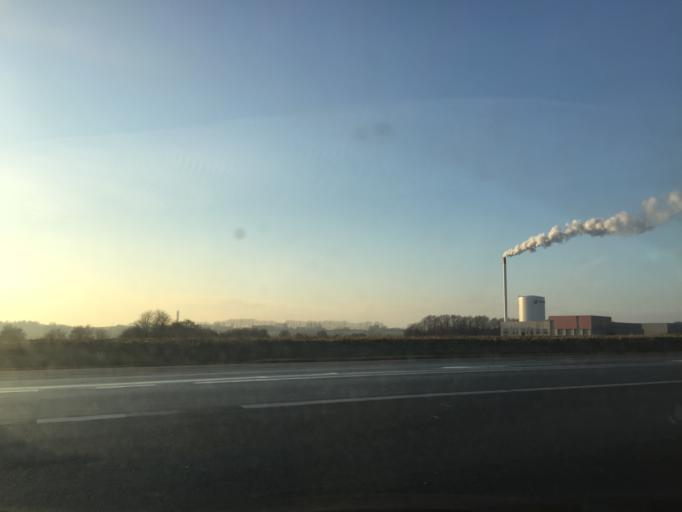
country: DK
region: Zealand
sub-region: Slagelse Kommune
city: Slagelse
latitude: 55.3818
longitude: 11.3725
